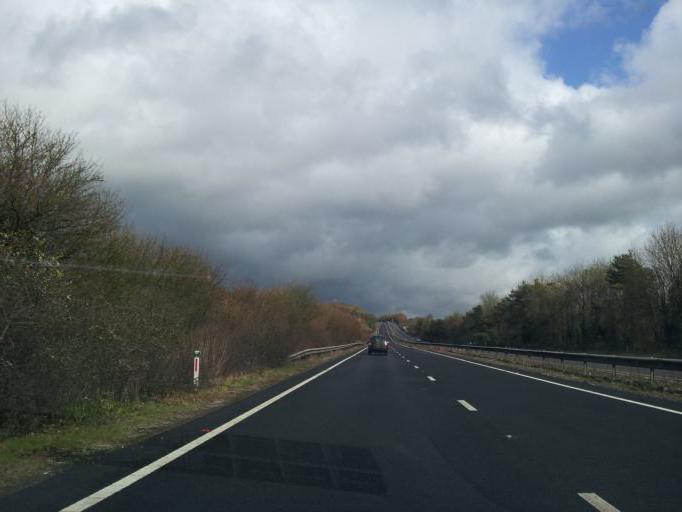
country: GB
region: England
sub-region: Somerset
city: Castle Cary
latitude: 51.0413
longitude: -2.4709
